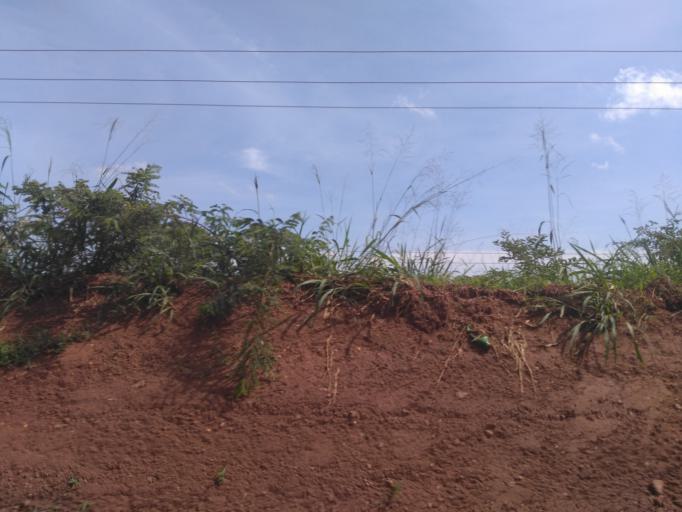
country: UG
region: Central Region
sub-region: Wakiso District
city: Kireka
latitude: 0.4424
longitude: 32.5867
